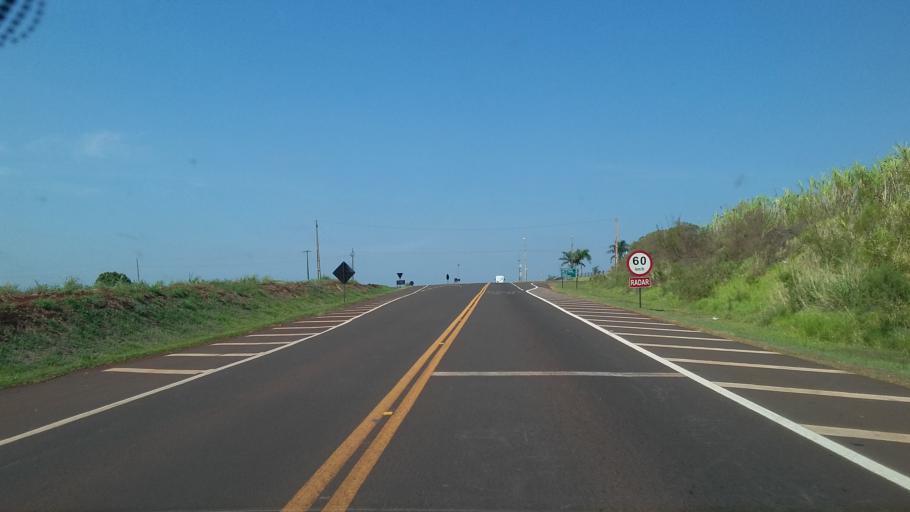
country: BR
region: Parana
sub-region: Bandeirantes
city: Bandeirantes
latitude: -23.1239
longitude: -50.3565
